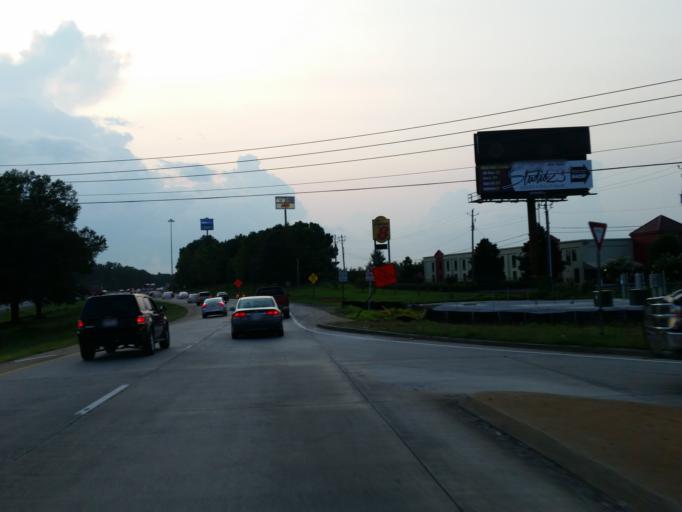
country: US
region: Georgia
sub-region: Henry County
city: McDonough
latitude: 33.4281
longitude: -84.1812
